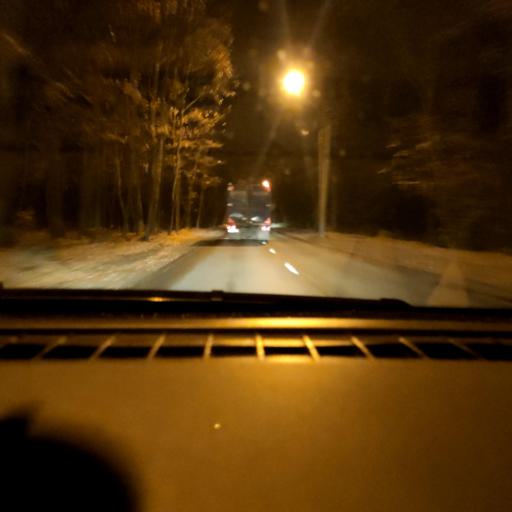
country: RU
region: Voronezj
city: Voronezh
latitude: 51.7178
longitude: 39.2253
